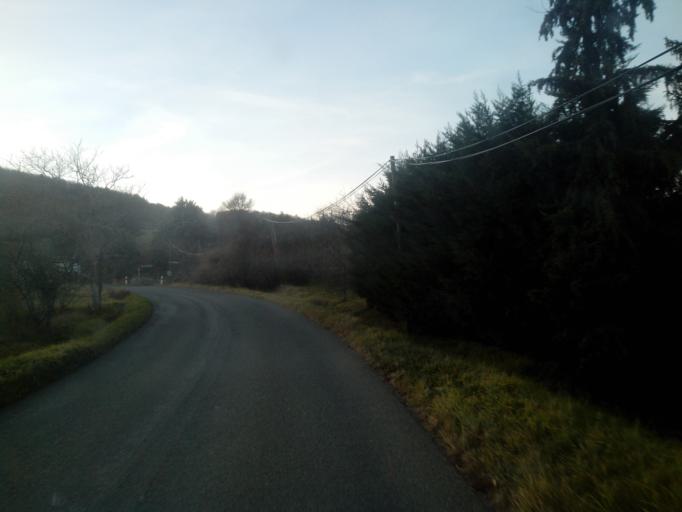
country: FR
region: Languedoc-Roussillon
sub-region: Departement de l'Aude
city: Chalabre
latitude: 42.9233
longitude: 2.0445
